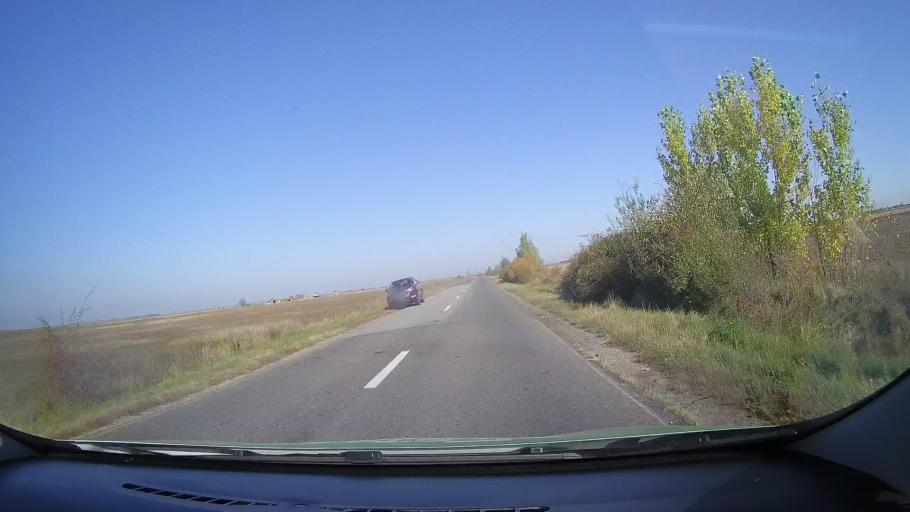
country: RO
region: Satu Mare
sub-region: Comuna Cauas
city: Cauas
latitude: 47.5306
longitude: 22.5668
